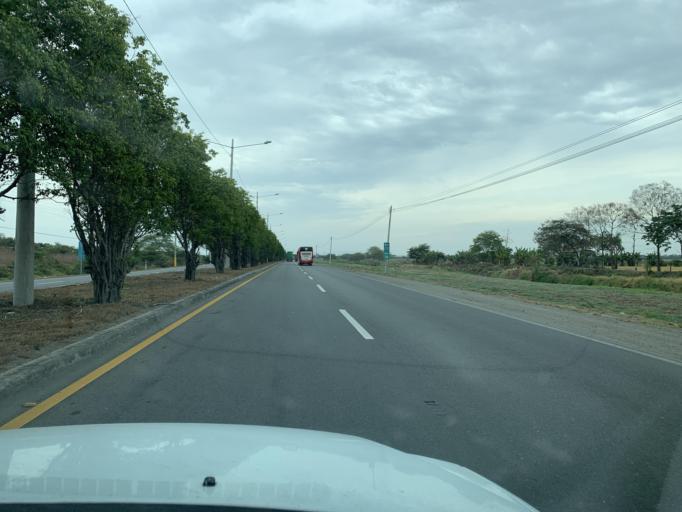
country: EC
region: Guayas
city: Yaguachi Nuevo
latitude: -2.2096
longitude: -79.7285
